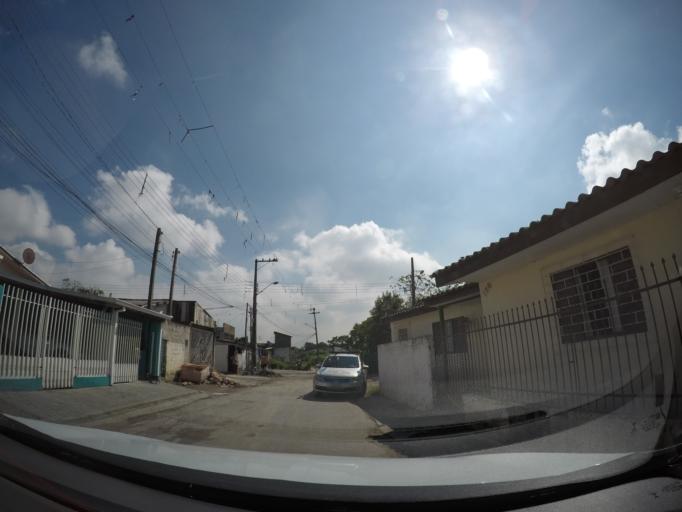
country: BR
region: Parana
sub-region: Sao Jose Dos Pinhais
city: Sao Jose dos Pinhais
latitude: -25.4983
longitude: -49.2236
